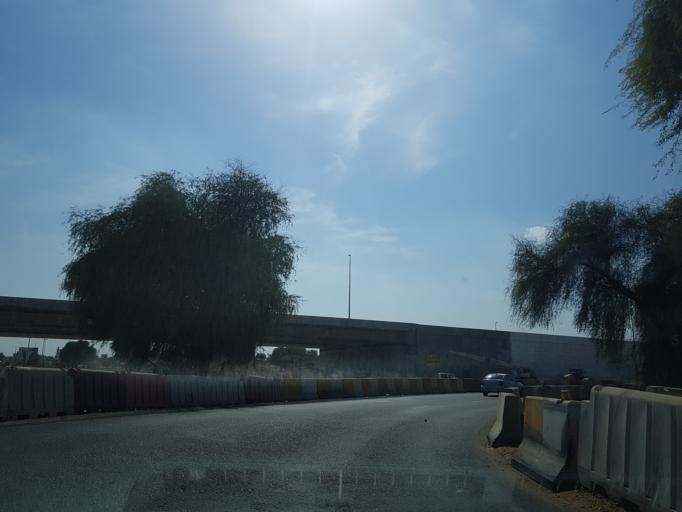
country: AE
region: Ra's al Khaymah
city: Ras al-Khaimah
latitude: 25.7010
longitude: 55.9677
